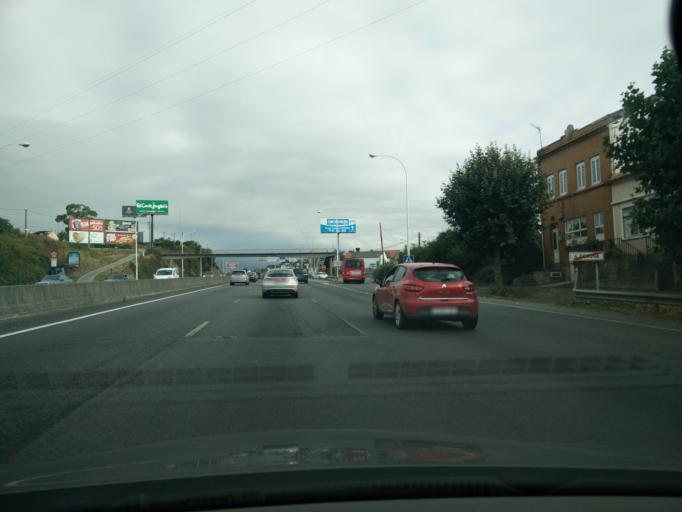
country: ES
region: Galicia
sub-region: Provincia da Coruna
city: A Coruna
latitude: 43.3365
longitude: -8.4041
